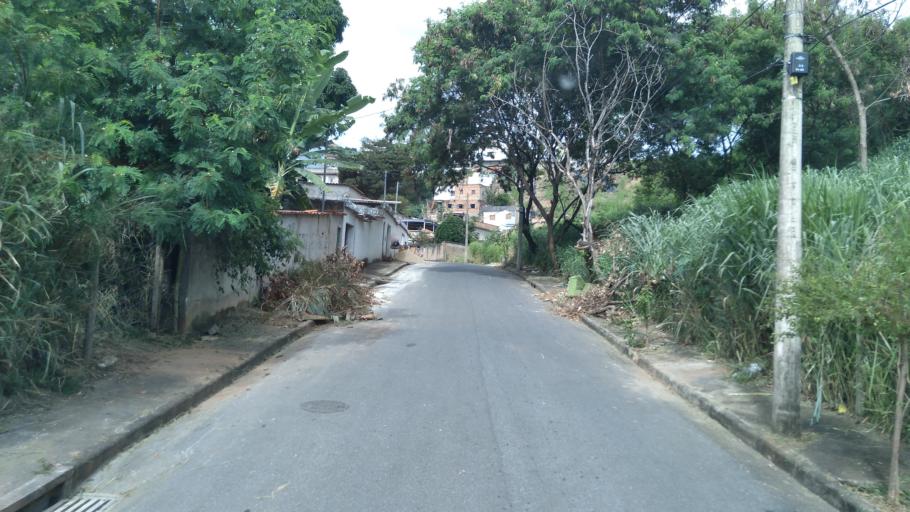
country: BR
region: Minas Gerais
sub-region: Belo Horizonte
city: Belo Horizonte
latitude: -19.8597
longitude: -43.9123
